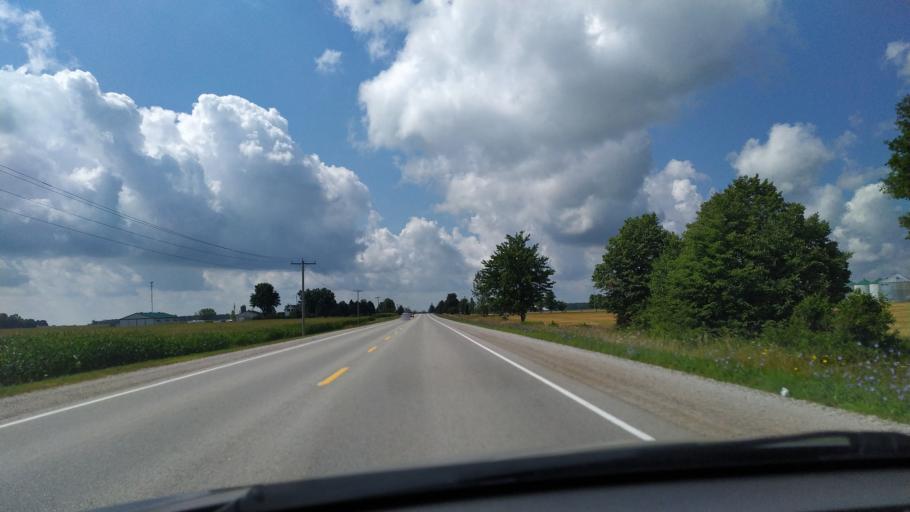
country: CA
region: Ontario
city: Huron East
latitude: 43.4164
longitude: -81.2419
